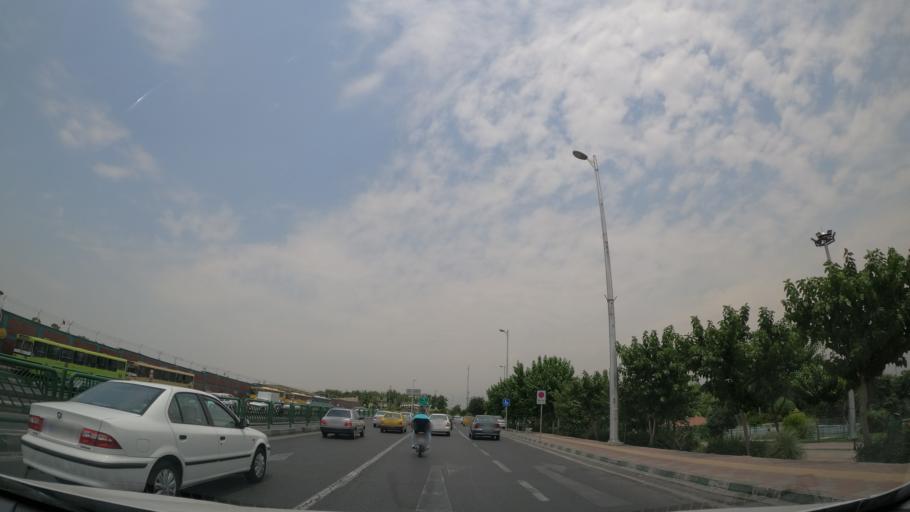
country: IR
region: Tehran
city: Tehran
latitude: 35.6961
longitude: 51.3395
